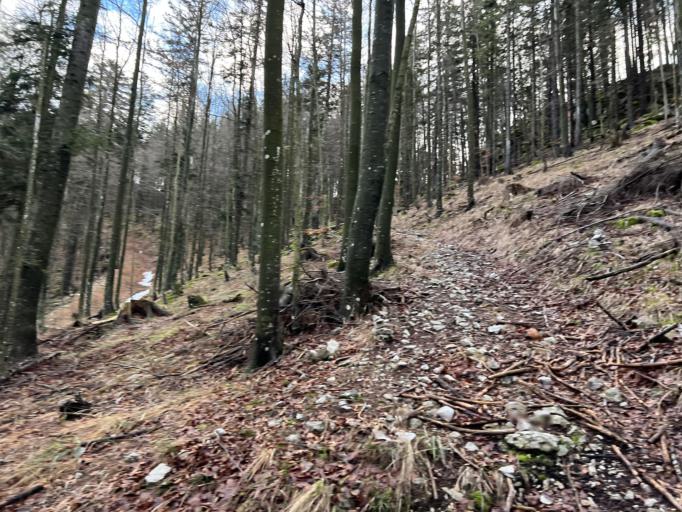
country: SI
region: Nova Gorica
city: Sempas
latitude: 45.9882
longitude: 13.8136
